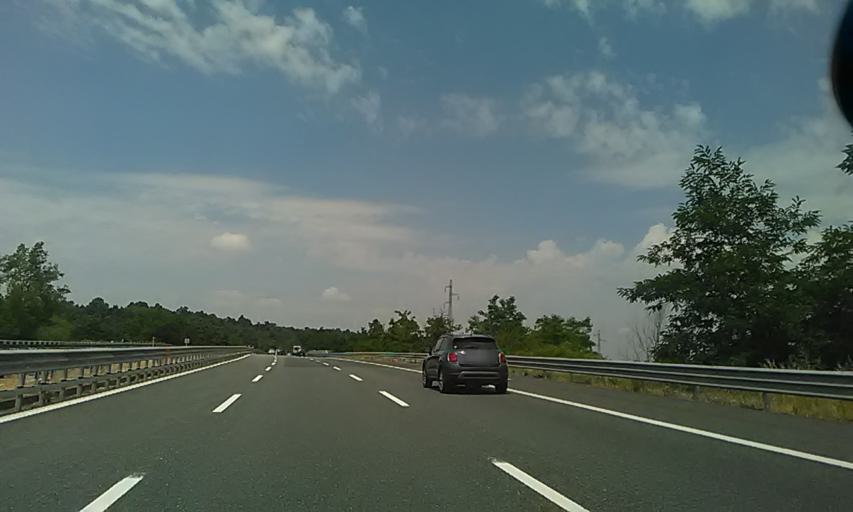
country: IT
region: Piedmont
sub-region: Provincia di Alessandria
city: Predosa
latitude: 44.7371
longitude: 8.6572
